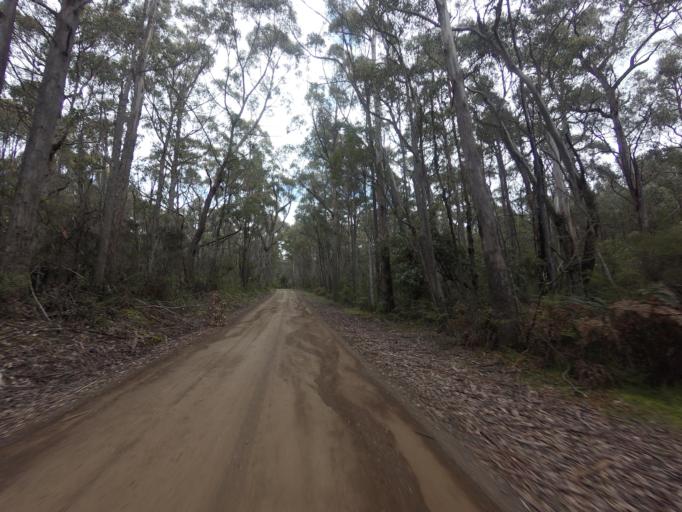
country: AU
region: Tasmania
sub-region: Huon Valley
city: Geeveston
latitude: -43.4244
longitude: 147.0070
